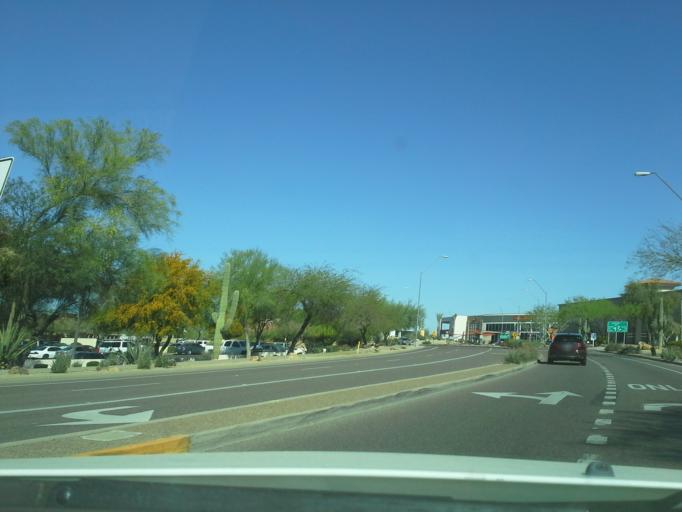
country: US
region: Arizona
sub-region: Maricopa County
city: Paradise Valley
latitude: 33.6259
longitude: -111.8949
